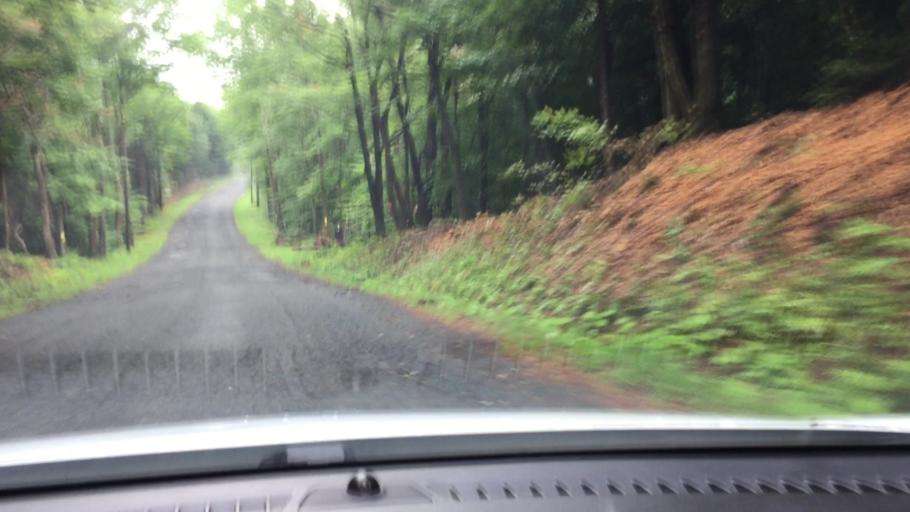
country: US
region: Massachusetts
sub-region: Berkshire County
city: Hinsdale
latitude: 42.4240
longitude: -73.0495
